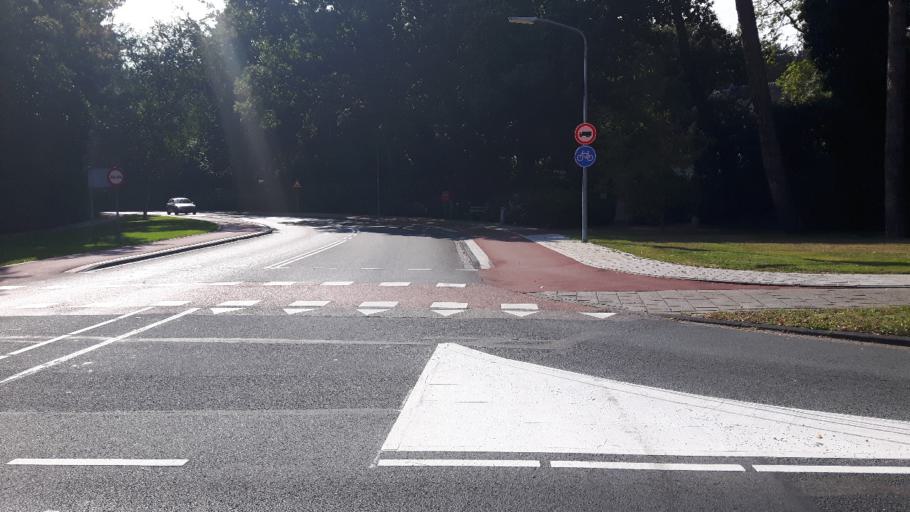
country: NL
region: North Holland
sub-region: Gemeente Heemstede
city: Heemstede
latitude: 52.3629
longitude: 4.5857
